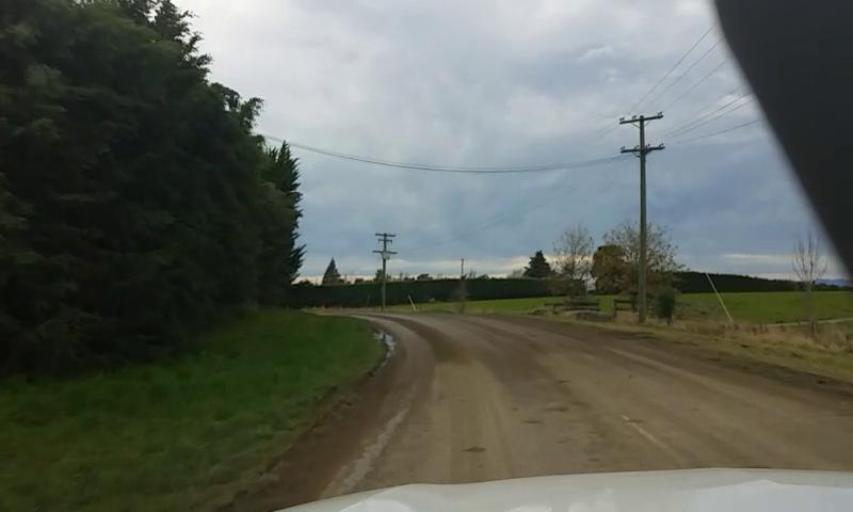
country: NZ
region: Canterbury
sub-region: Waimakariri District
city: Kaiapoi
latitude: -43.2999
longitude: 172.4834
